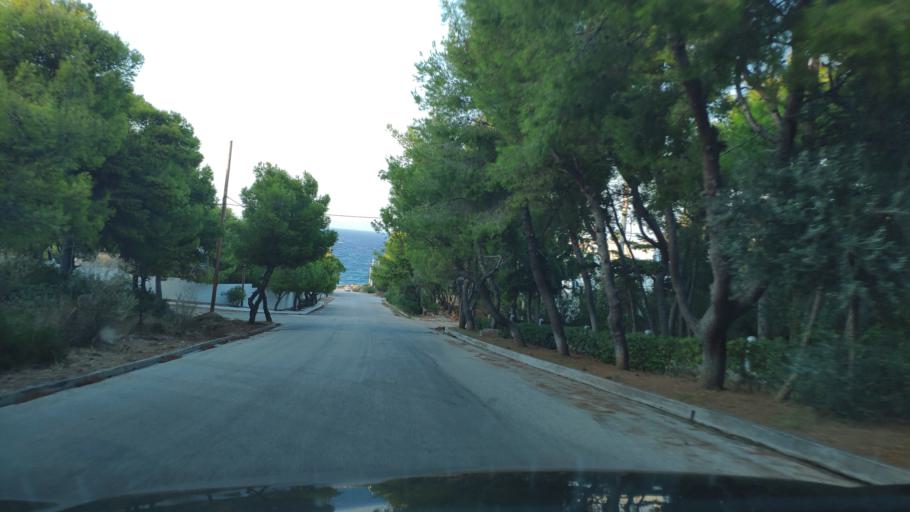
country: GR
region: Attica
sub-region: Nomarchia Anatolikis Attikis
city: Limin Mesoyaias
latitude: 37.9187
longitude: 24.0238
